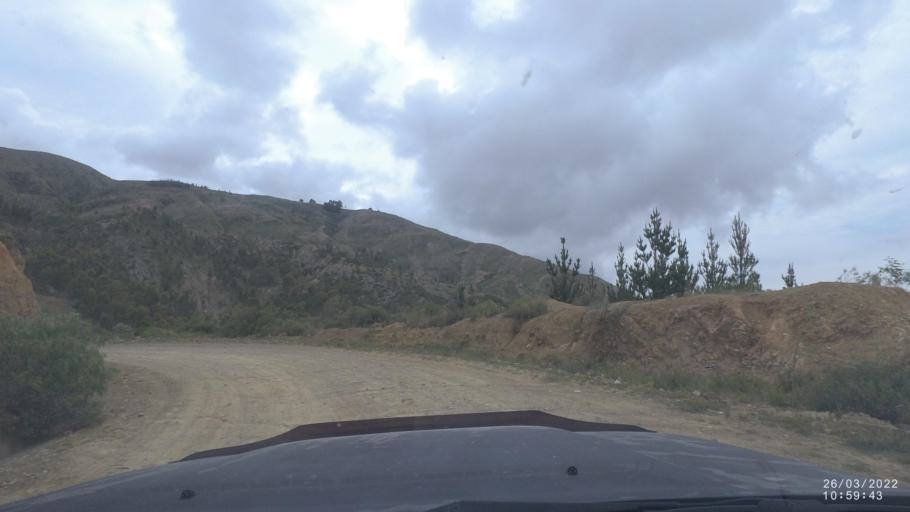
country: BO
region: Cochabamba
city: Tarata
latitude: -17.5152
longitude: -66.0251
